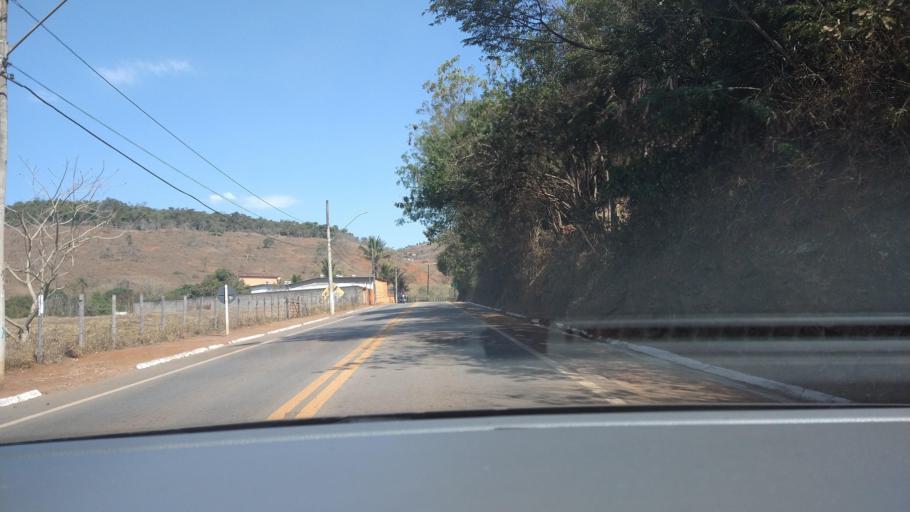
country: BR
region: Minas Gerais
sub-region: Rio Piracicaba
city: Rio Piracicaba
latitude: -19.9240
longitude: -43.1639
